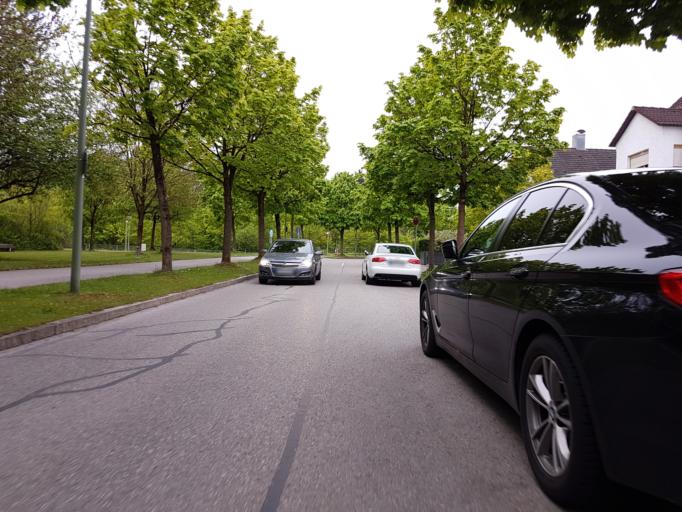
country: DE
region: Bavaria
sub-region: Upper Bavaria
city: Karlsfeld
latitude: 48.2094
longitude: 11.4624
